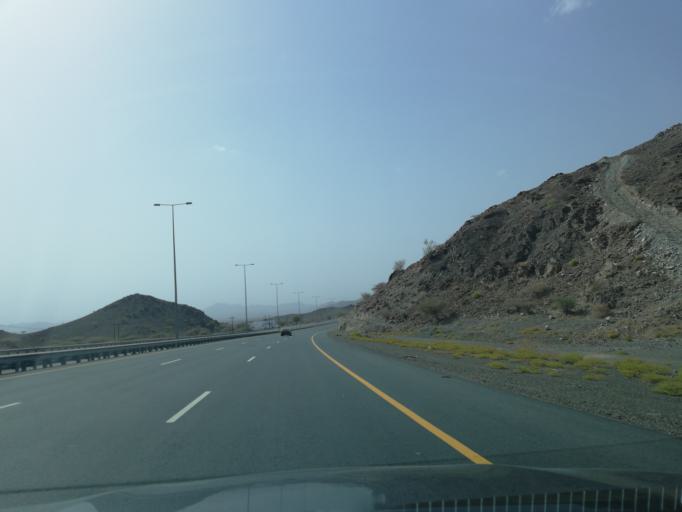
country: OM
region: Ash Sharqiyah
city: Ibra'
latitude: 22.8948
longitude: 58.2762
